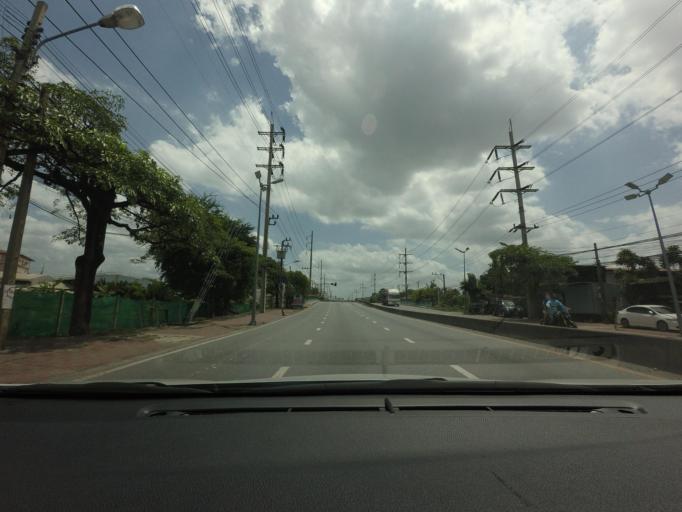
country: TH
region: Samut Prakan
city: Phra Pradaeng
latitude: 13.6508
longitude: 100.5548
